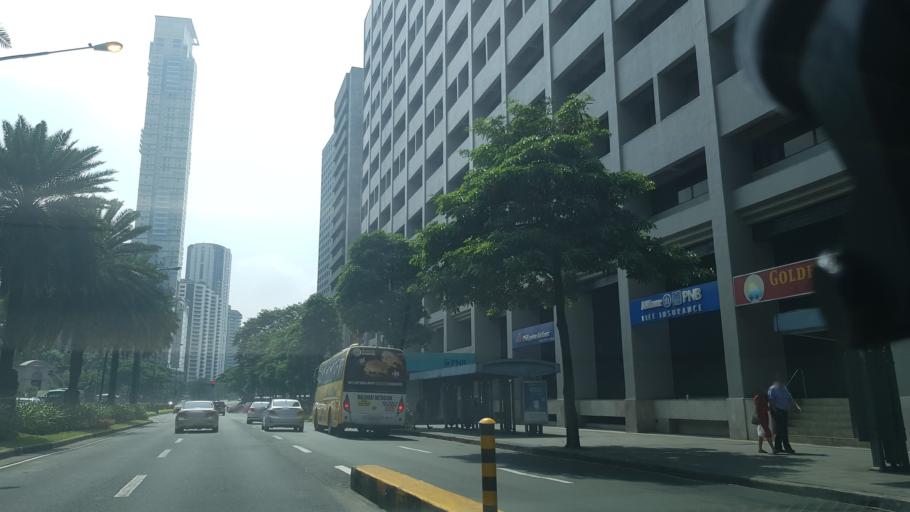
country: PH
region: Metro Manila
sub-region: Makati City
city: Makati City
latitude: 14.5556
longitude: 121.0230
